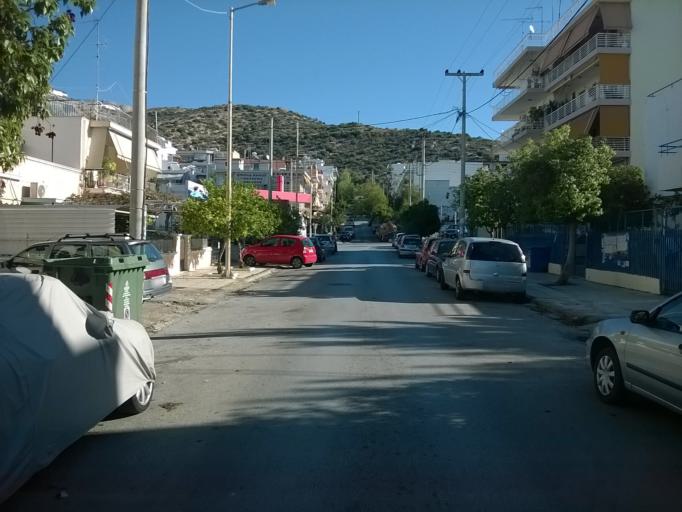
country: GR
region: Attica
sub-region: Nomarchia Athinas
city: Argyroupoli
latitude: 37.9000
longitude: 23.7558
